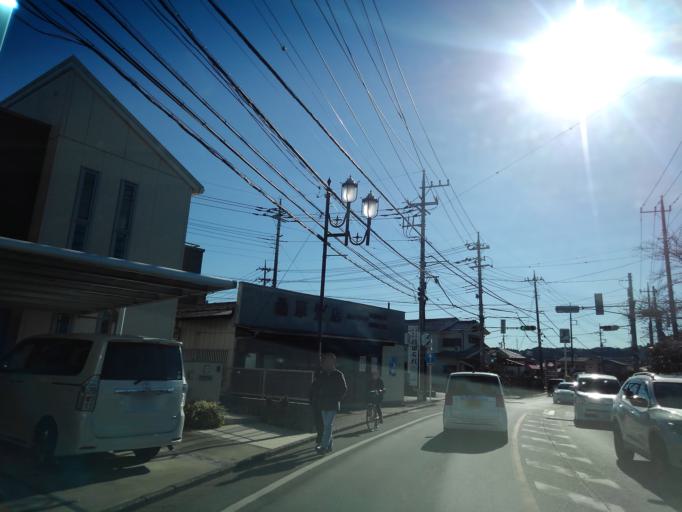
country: JP
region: Saitama
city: Hanno
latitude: 35.8478
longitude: 139.3208
